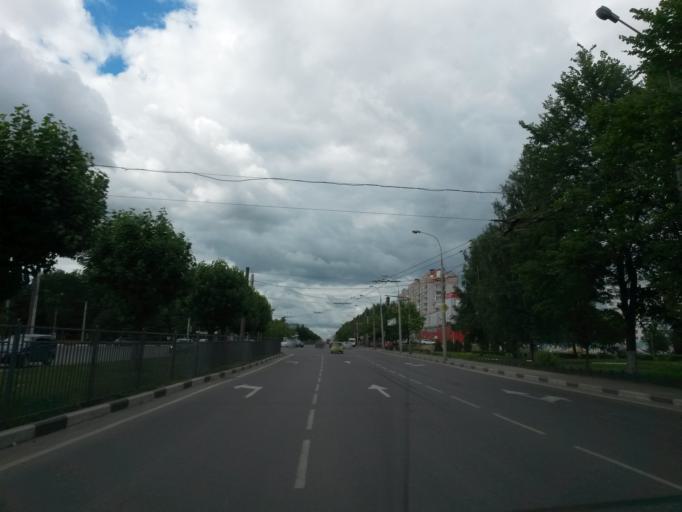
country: RU
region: Jaroslavl
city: Yaroslavl
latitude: 57.6850
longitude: 39.7863
